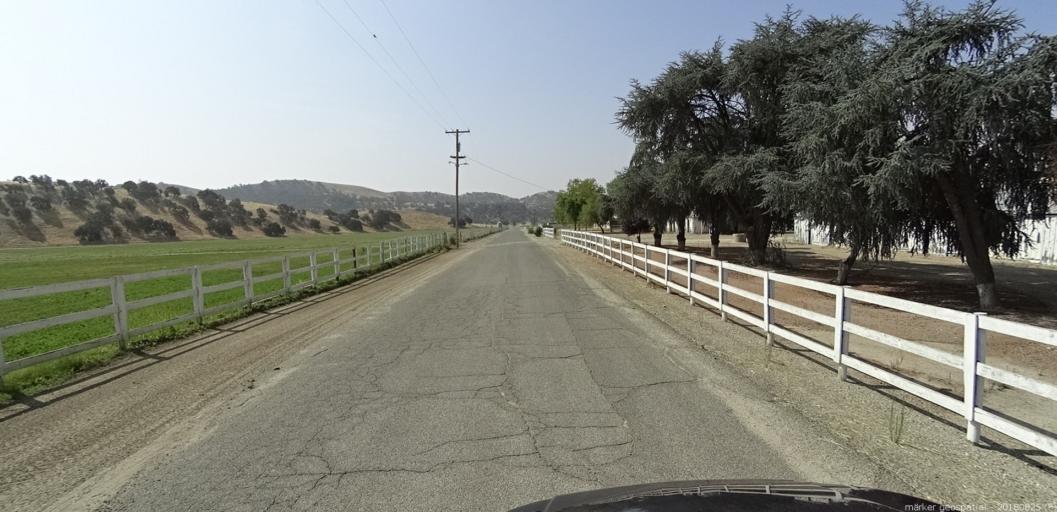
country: US
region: California
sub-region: San Luis Obispo County
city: San Miguel
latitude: 35.8328
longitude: -120.6555
